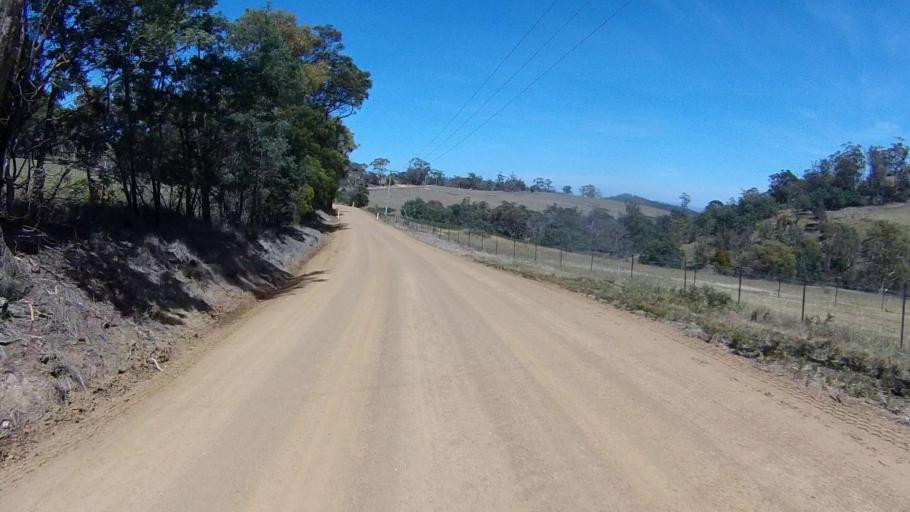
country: AU
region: Tasmania
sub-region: Sorell
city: Sorell
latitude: -42.7797
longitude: 147.6498
